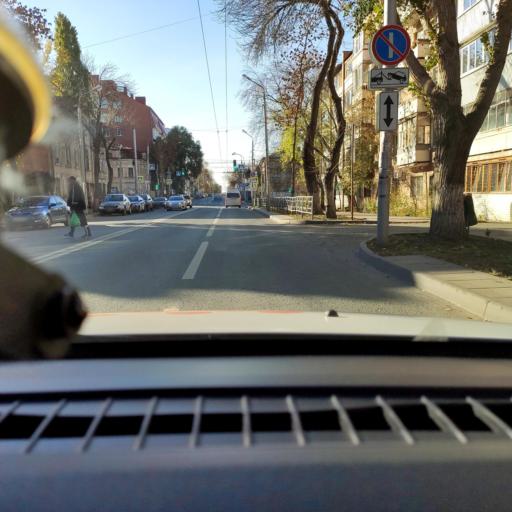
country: RU
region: Samara
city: Rozhdestveno
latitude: 53.1833
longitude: 50.0786
